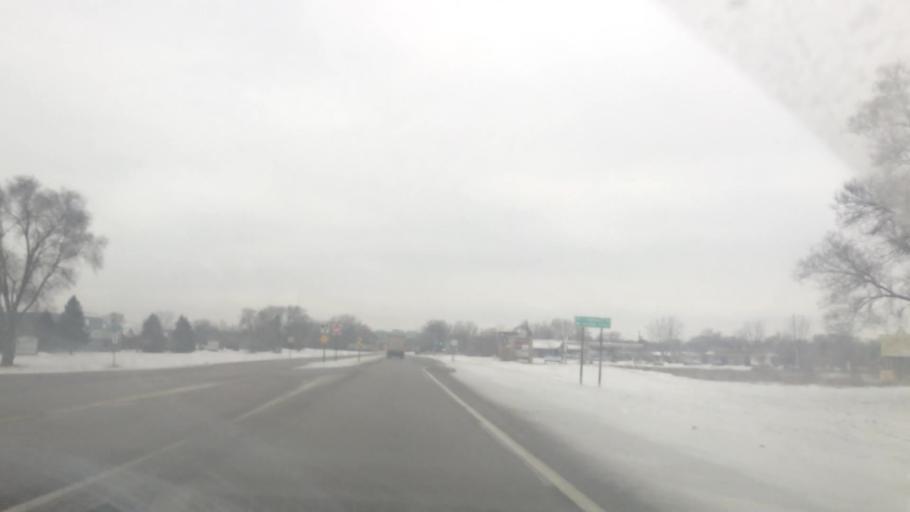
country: US
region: Minnesota
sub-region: Anoka County
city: Lexington
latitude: 45.1315
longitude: -93.1799
